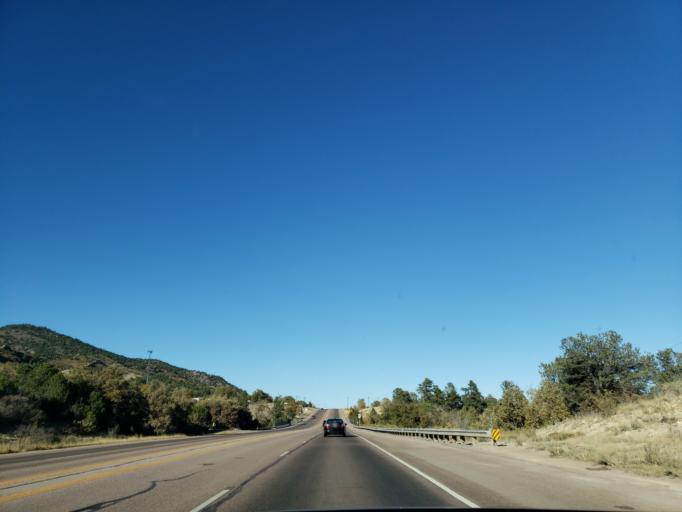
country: US
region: Colorado
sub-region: El Paso County
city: Fort Carson
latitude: 38.6755
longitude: -104.8501
